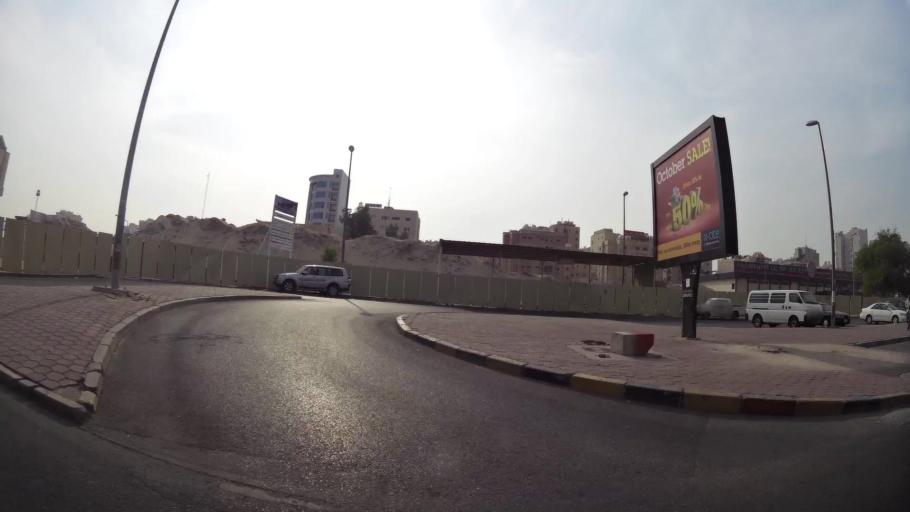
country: KW
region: Al Farwaniyah
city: Al Farwaniyah
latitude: 29.2788
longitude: 47.9616
